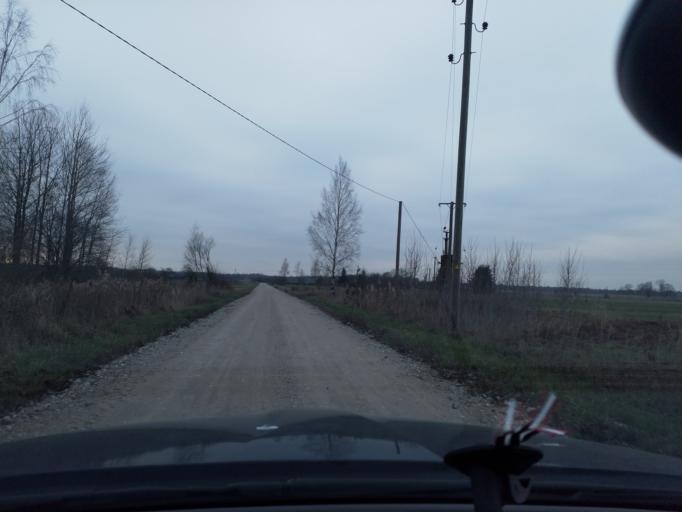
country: LV
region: Rucavas
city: Rucava
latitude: 56.2452
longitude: 21.2496
